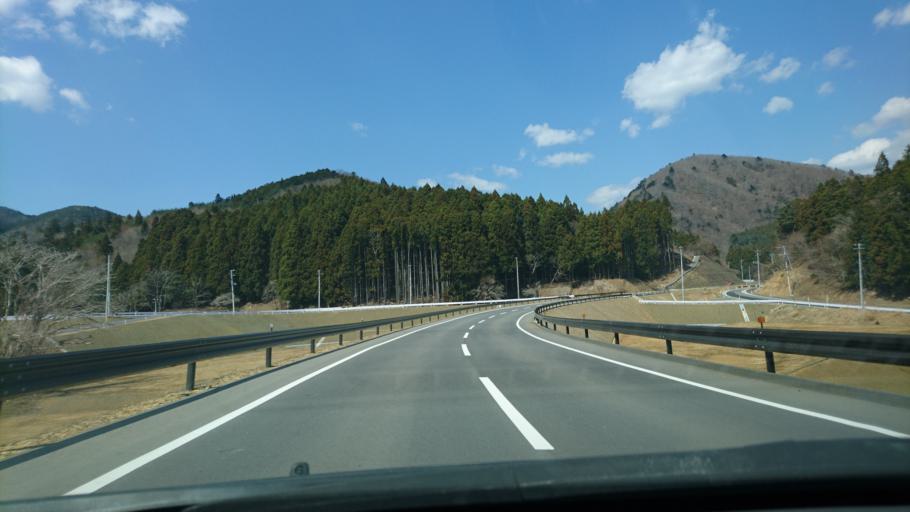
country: JP
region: Miyagi
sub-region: Oshika Gun
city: Onagawa Cho
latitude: 38.4635
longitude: 141.4735
